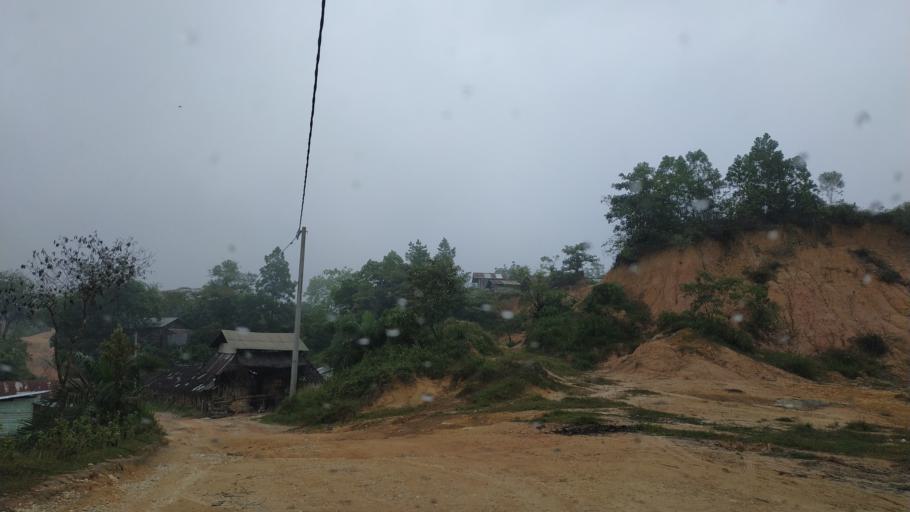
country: ID
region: Riau
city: Pekanbaru
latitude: 0.5012
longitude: 101.5298
